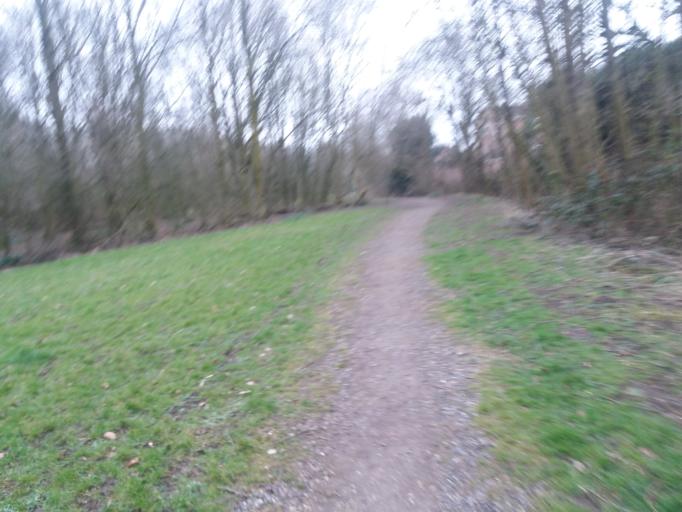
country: GB
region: England
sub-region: Lancashire
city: Chorley
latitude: 53.6683
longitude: -2.6268
